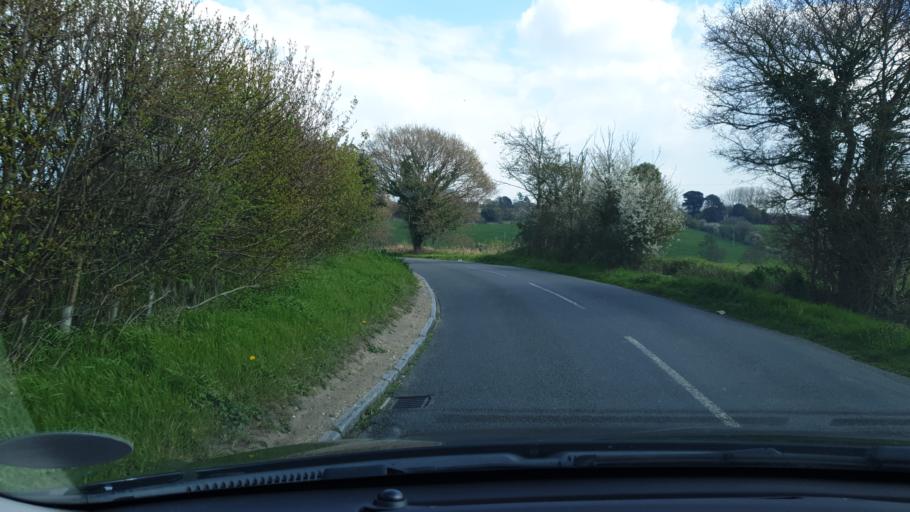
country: GB
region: England
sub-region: Essex
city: Great Bentley
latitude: 51.8710
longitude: 1.1063
